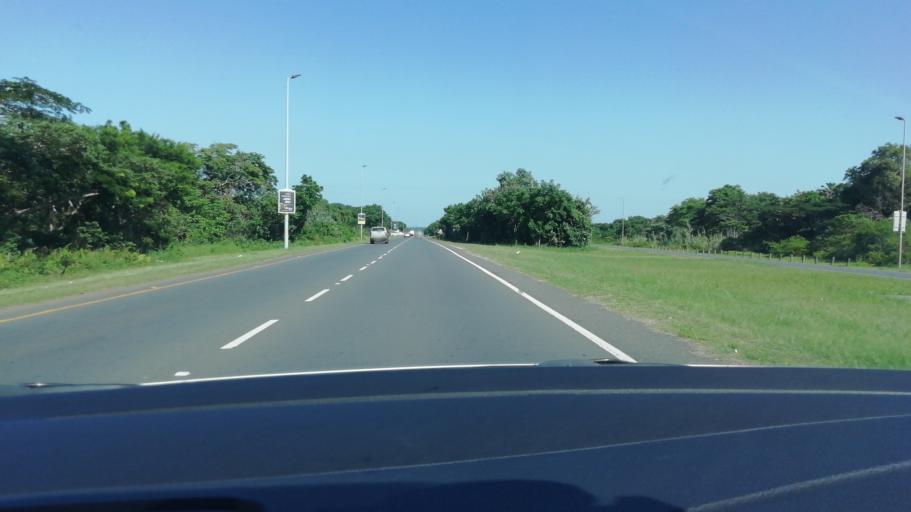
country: ZA
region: KwaZulu-Natal
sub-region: uThungulu District Municipality
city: Richards Bay
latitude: -28.7852
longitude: 32.0876
